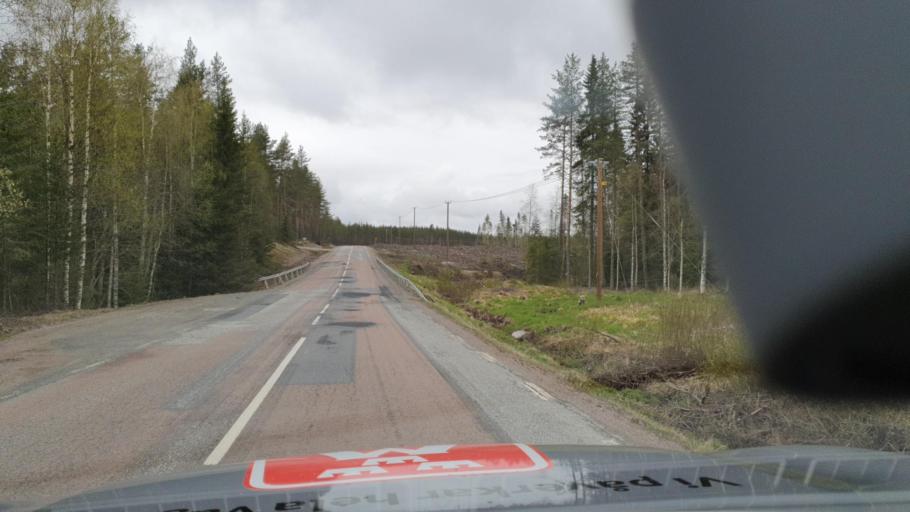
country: SE
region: Vaesternorrland
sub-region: Solleftea Kommun
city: Solleftea
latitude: 63.6132
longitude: 17.5186
